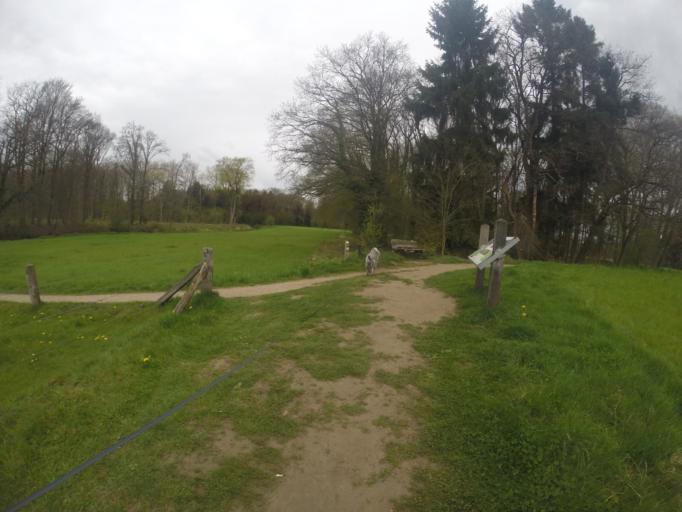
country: NL
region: Gelderland
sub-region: Gemeente Zutphen
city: Leesten
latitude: 52.1019
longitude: 6.2740
